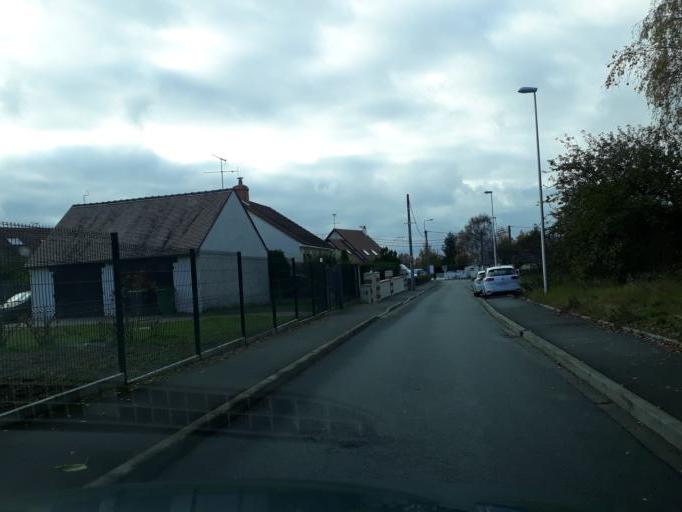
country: FR
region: Centre
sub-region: Departement du Loiret
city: Saint-Jean-de-la-Ruelle
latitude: 47.9317
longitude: 1.8591
